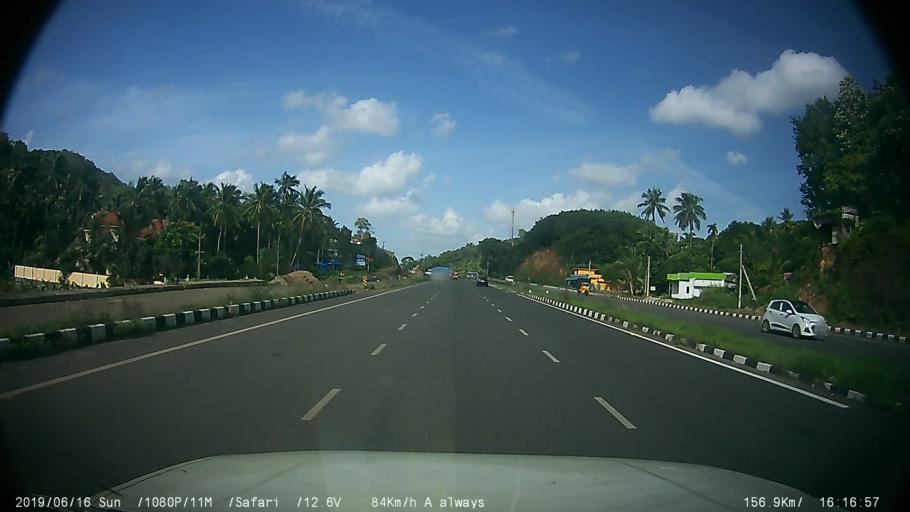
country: IN
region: Kerala
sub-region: Thrissur District
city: Chelakara
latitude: 10.5768
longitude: 76.4041
